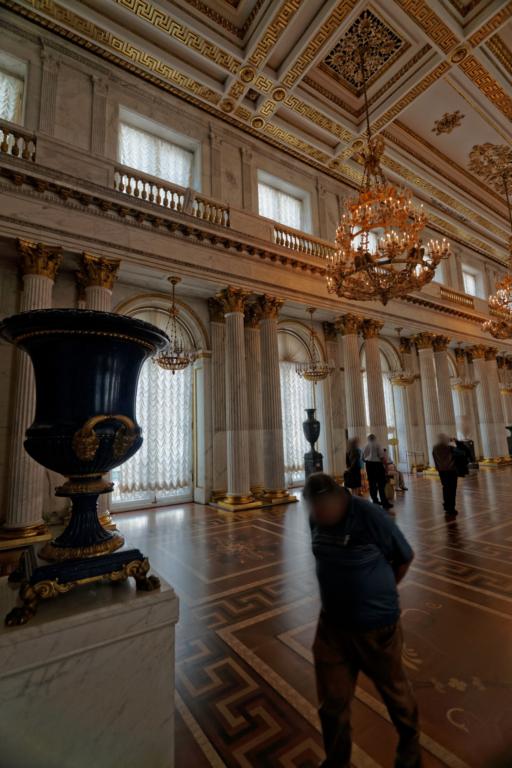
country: RU
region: St.-Petersburg
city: Saint Petersburg
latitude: 59.9408
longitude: 30.3148
